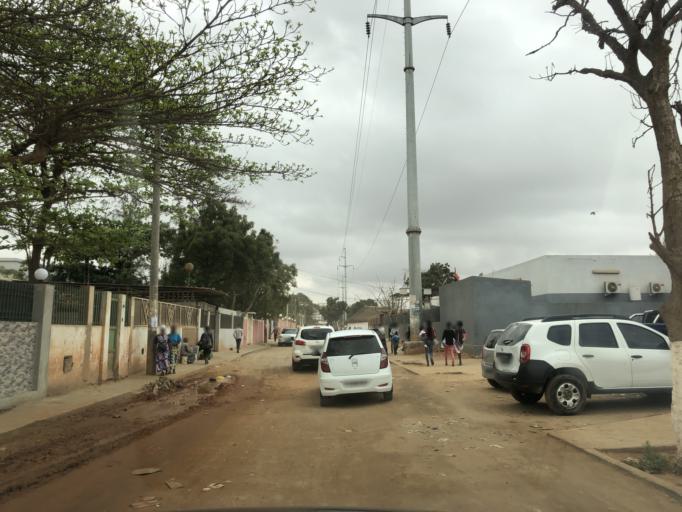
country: AO
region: Luanda
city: Luanda
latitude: -8.8975
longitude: 13.1962
